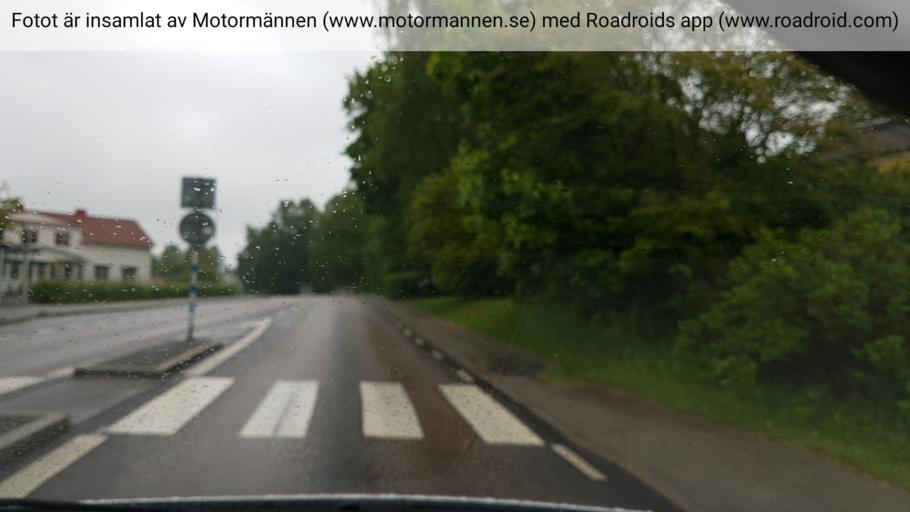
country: SE
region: Vaestra Goetaland
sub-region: Ulricehamns Kommun
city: Ulricehamn
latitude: 57.9332
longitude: 13.4972
